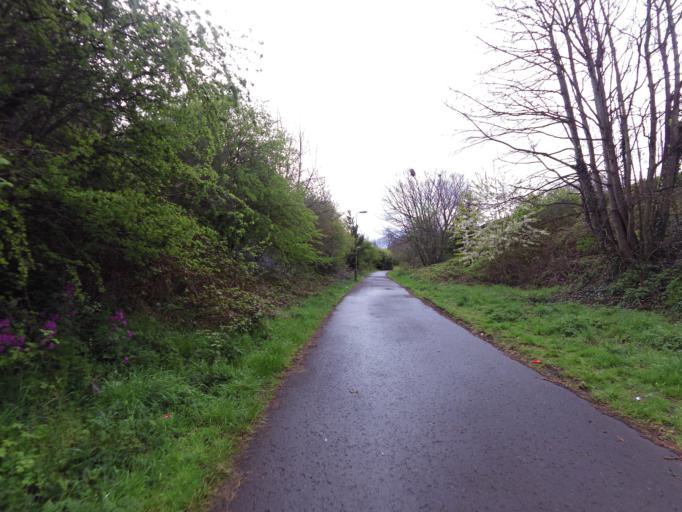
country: GB
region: Scotland
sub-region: Edinburgh
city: Edinburgh
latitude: 55.9601
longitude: -3.2472
